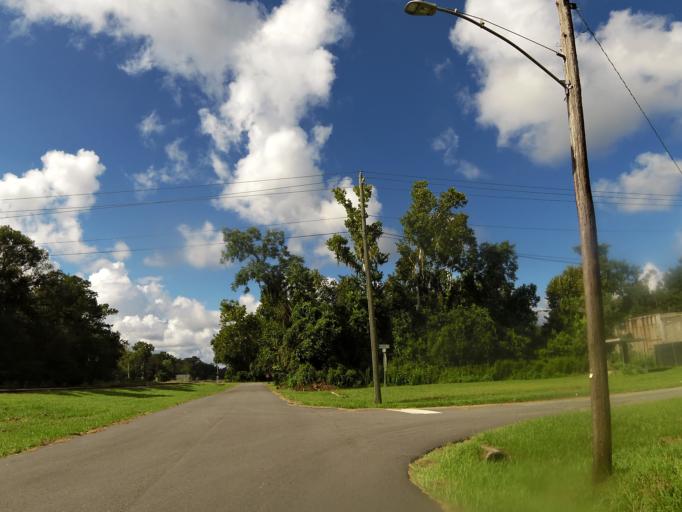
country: US
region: Georgia
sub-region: Camden County
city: Kingsland
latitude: 30.8009
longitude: -81.6912
